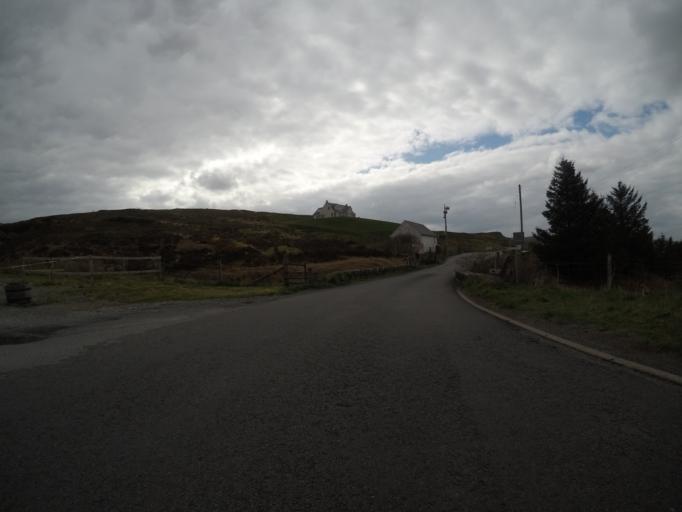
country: GB
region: Scotland
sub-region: Highland
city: Isle of Skye
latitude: 57.2949
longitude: -6.3347
